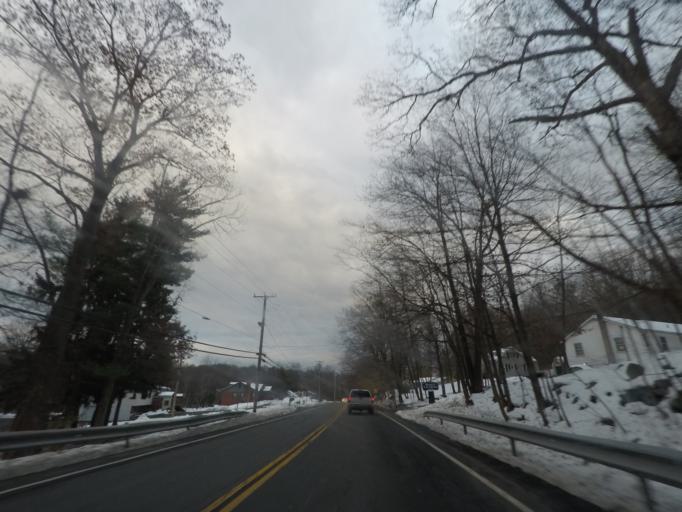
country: US
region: New York
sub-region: Orange County
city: Gardnertown
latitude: 41.5411
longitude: -74.0446
